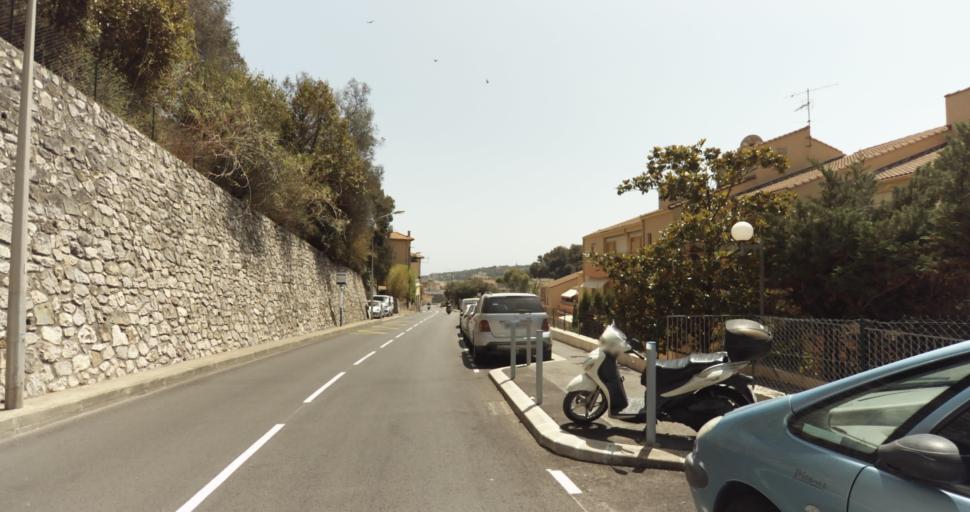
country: FR
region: Provence-Alpes-Cote d'Azur
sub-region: Departement des Alpes-Maritimes
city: Roquebrune-Cap-Martin
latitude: 43.7698
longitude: 7.4799
